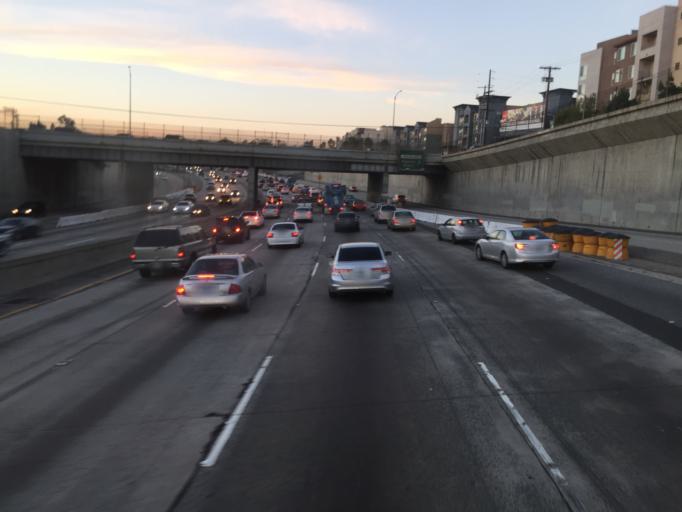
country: US
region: California
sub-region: Los Angeles County
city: Los Angeles
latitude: 34.0779
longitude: -118.2195
